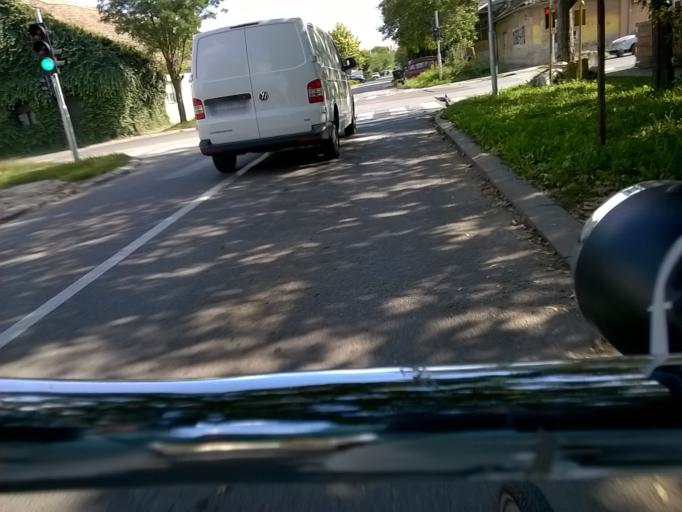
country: RS
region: Autonomna Pokrajina Vojvodina
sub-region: Juznobanatski Okrug
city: Pancevo
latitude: 44.8783
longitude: 20.6430
